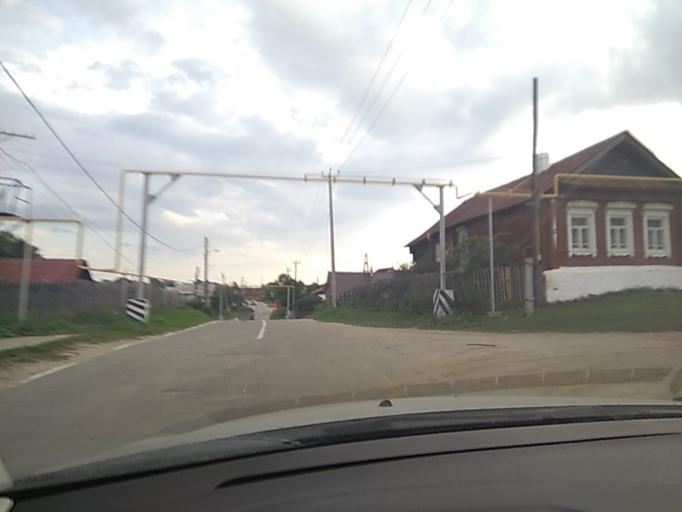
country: RU
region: Chelyabinsk
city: Kyshtym
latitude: 55.6961
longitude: 60.5318
